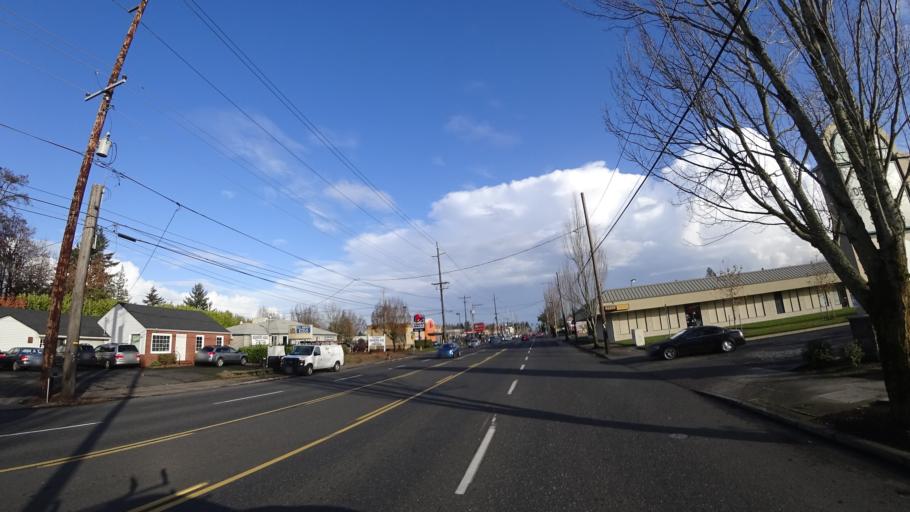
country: US
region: Oregon
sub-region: Multnomah County
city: Lents
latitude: 45.5263
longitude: -122.5405
